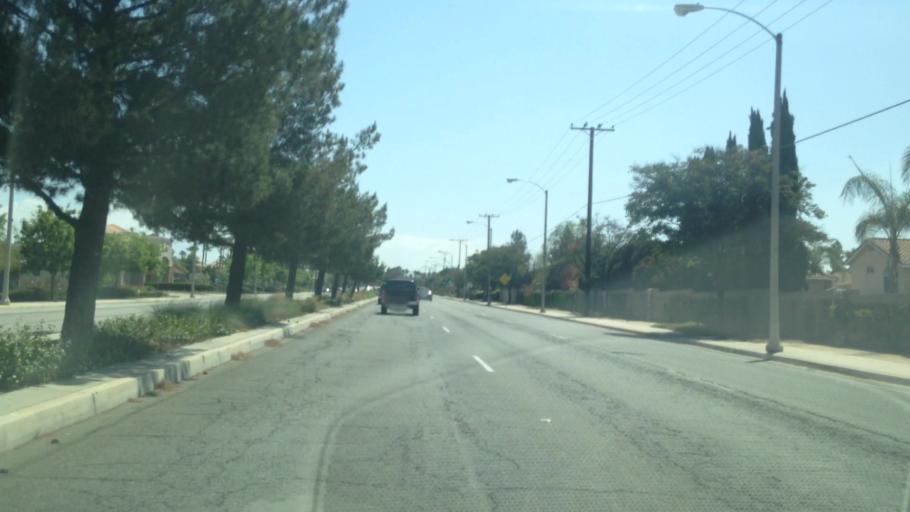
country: US
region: California
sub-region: Riverside County
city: Woodcrest
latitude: 33.8879
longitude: -117.3270
